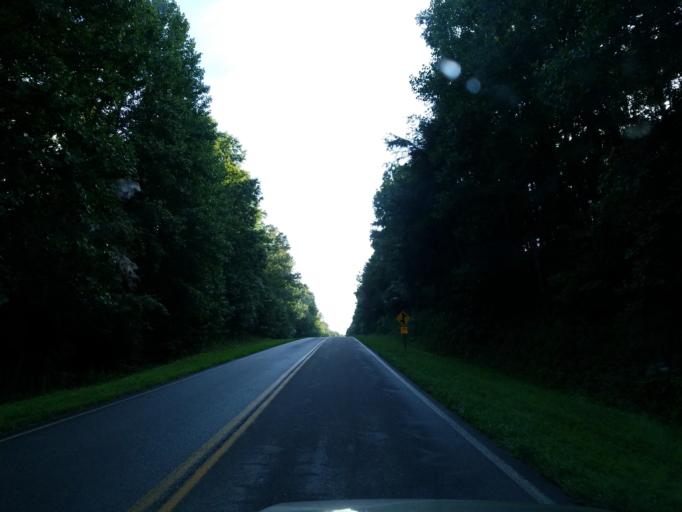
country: US
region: Georgia
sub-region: Lumpkin County
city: Dahlonega
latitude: 34.5390
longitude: -83.8919
